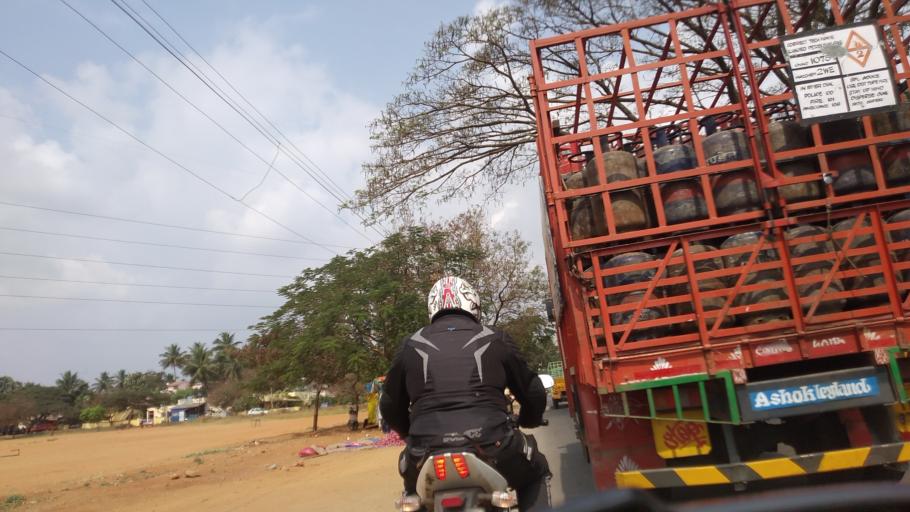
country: IN
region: Tamil Nadu
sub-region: Coimbatore
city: Perur
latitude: 10.9466
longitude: 76.9369
